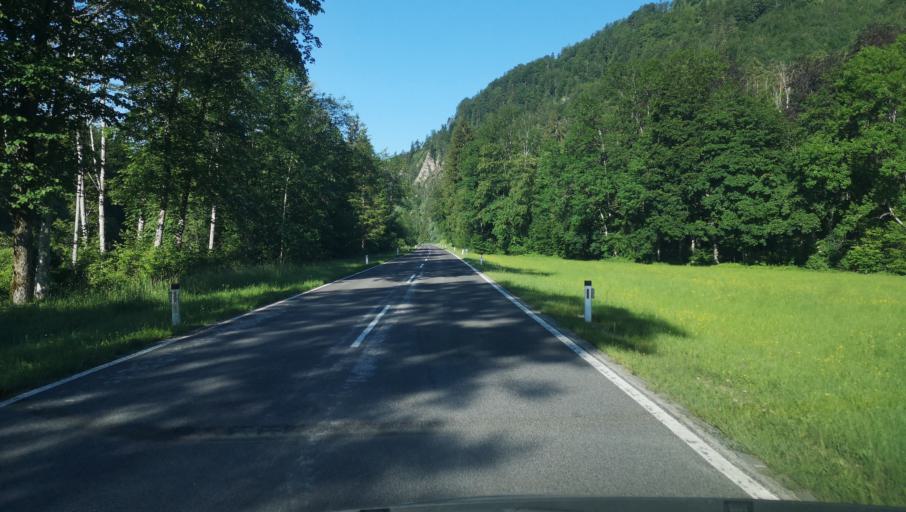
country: AT
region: Lower Austria
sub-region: Politischer Bezirk Amstetten
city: Opponitz
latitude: 47.8731
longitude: 14.7982
